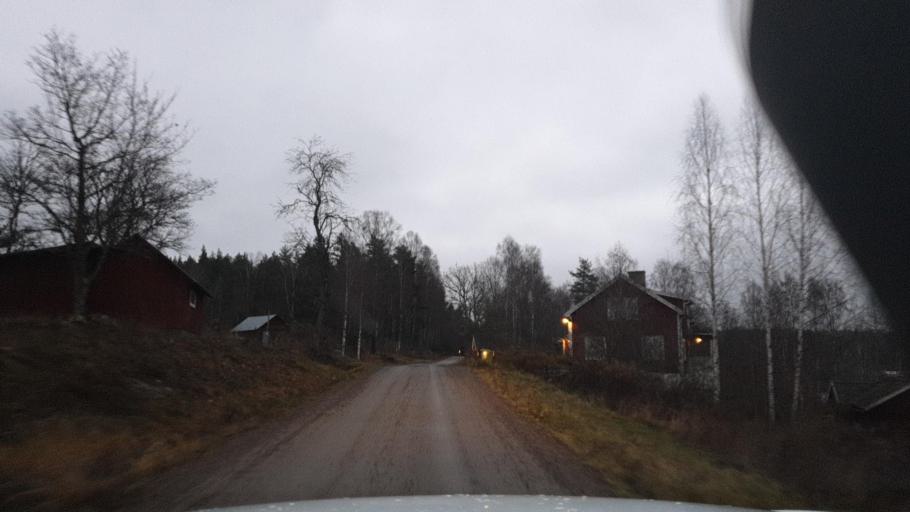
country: SE
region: Vaermland
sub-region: Eda Kommun
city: Amotfors
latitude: 59.8095
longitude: 12.4429
